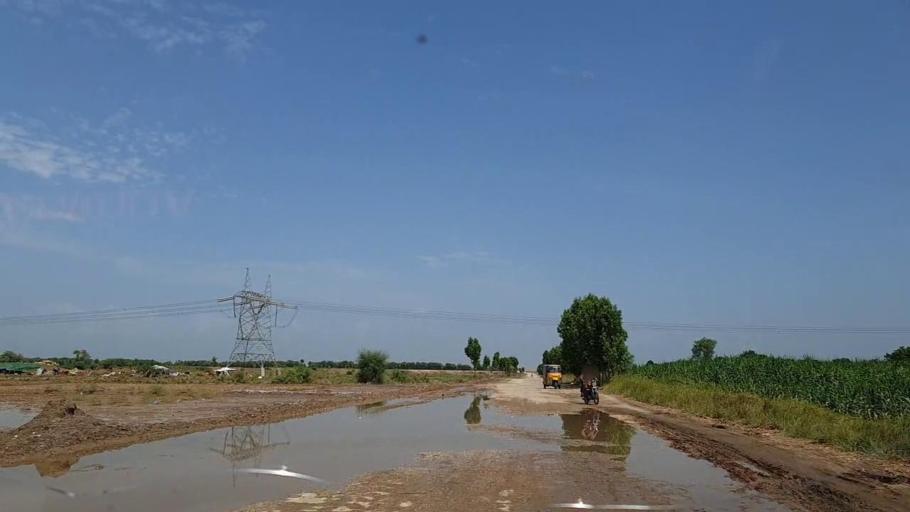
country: PK
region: Sindh
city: Naushahro Firoz
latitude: 26.8271
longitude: 68.1498
